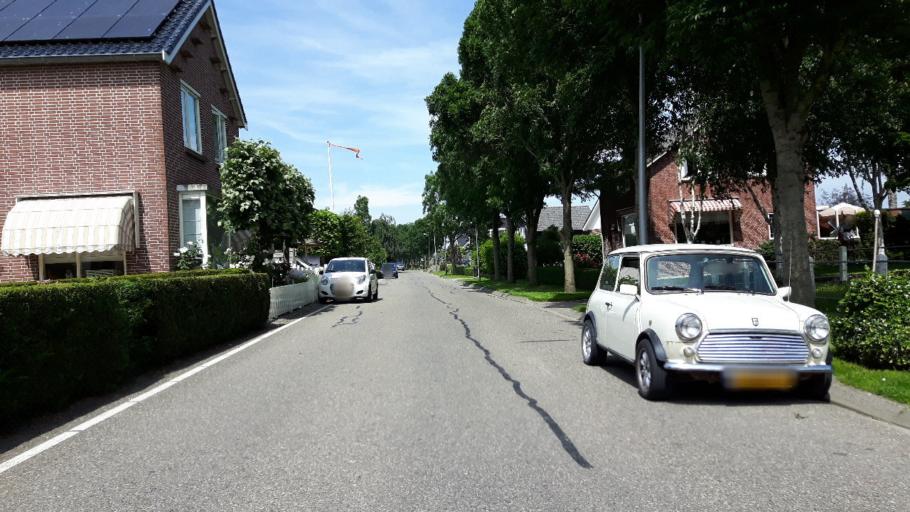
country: NL
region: South Holland
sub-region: Gemeente Nieuwkoop
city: Nieuwkoop
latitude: 52.1632
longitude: 4.7274
